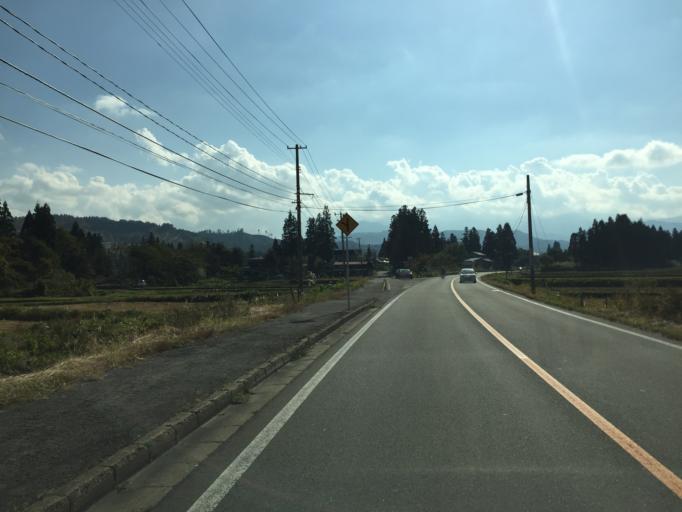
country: JP
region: Yamagata
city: Yonezawa
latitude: 37.9035
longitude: 140.0261
